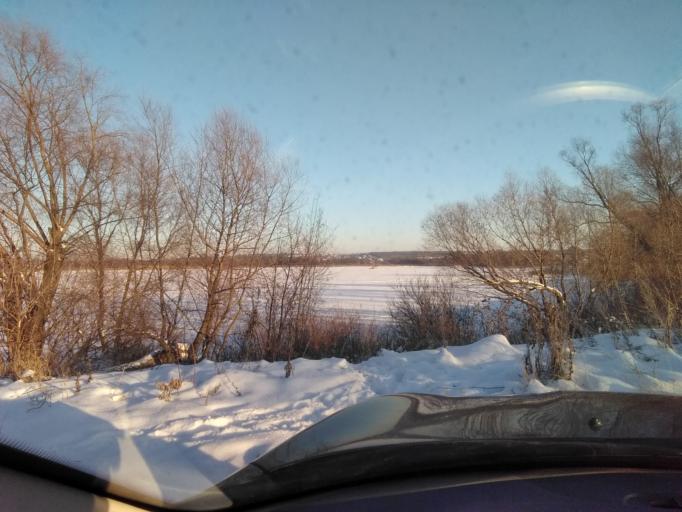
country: RU
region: Tatarstan
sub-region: Gorod Kazan'
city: Kazan
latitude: 55.8379
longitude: 49.1659
